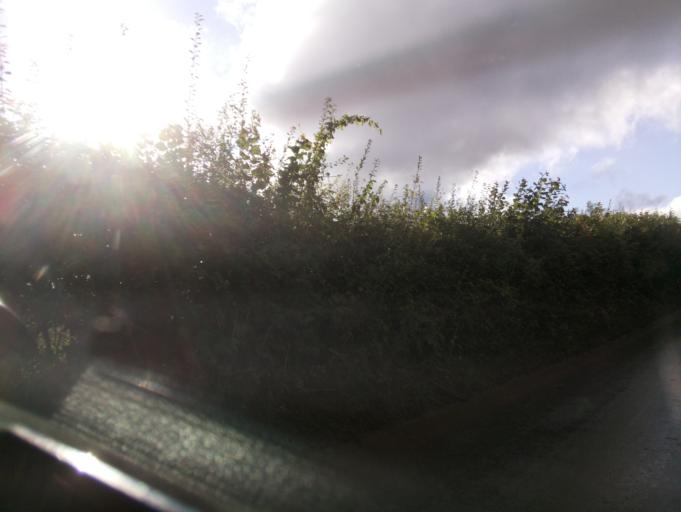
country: GB
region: England
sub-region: Devon
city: Totnes
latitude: 50.3702
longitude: -3.7431
